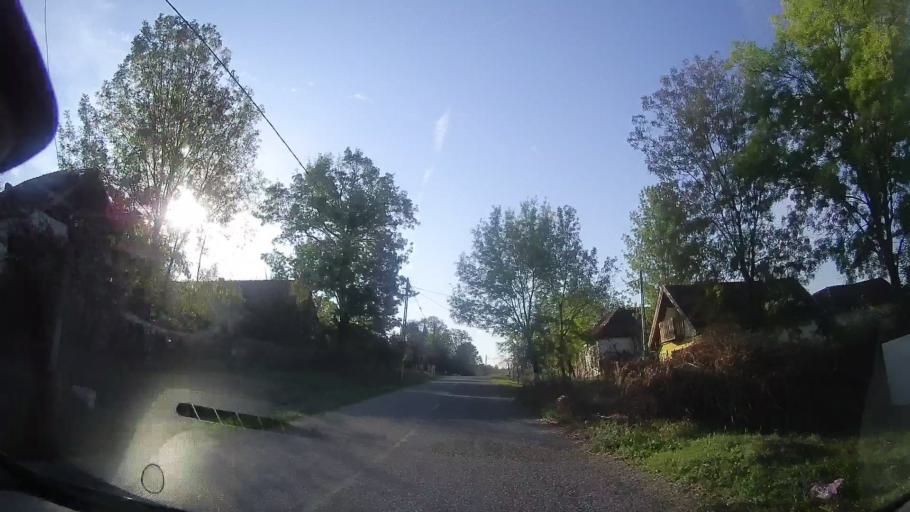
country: RO
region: Timis
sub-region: Comuna Bogda
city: Bogda
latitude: 45.9621
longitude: 21.6136
